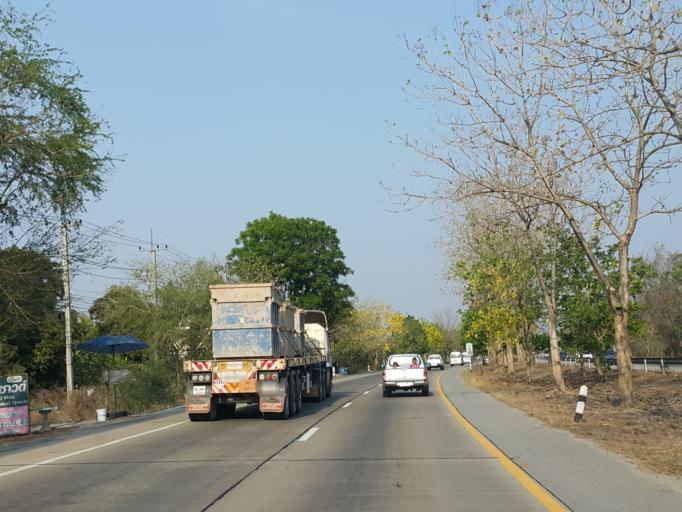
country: TH
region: Suphan Buri
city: Sam Chuk
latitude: 14.7888
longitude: 100.0945
